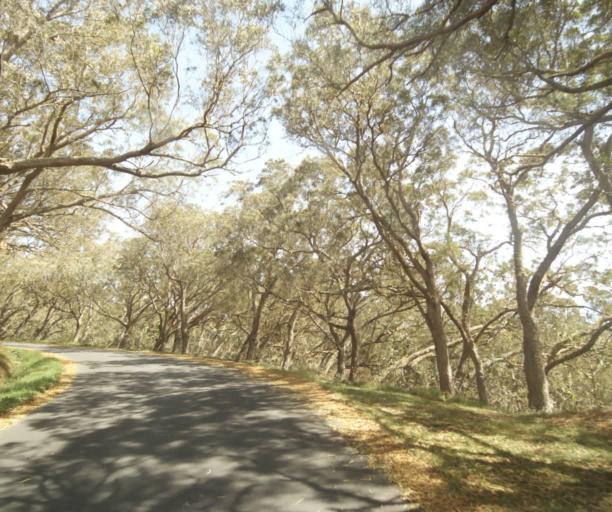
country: RE
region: Reunion
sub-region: Reunion
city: Trois-Bassins
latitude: -21.0593
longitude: 55.3691
